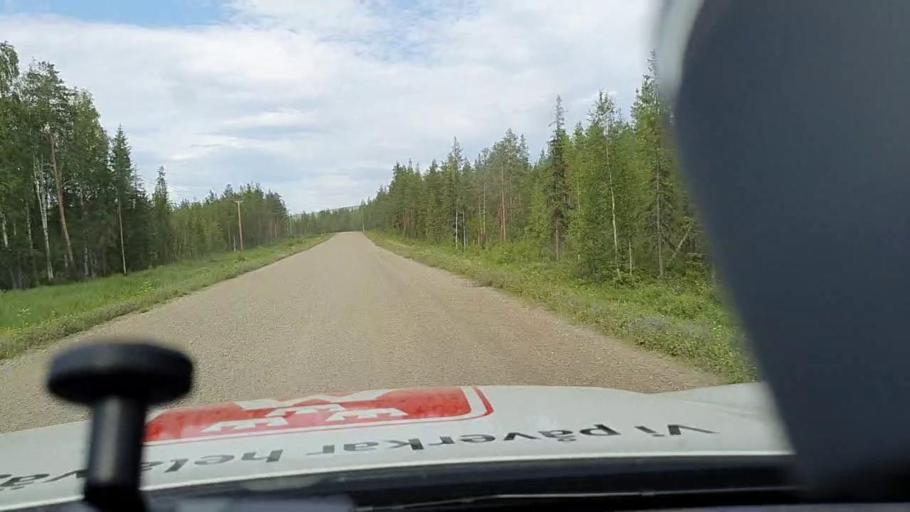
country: SE
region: Norrbotten
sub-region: Alvsbyns Kommun
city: AElvsbyn
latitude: 66.1401
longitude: 21.0107
